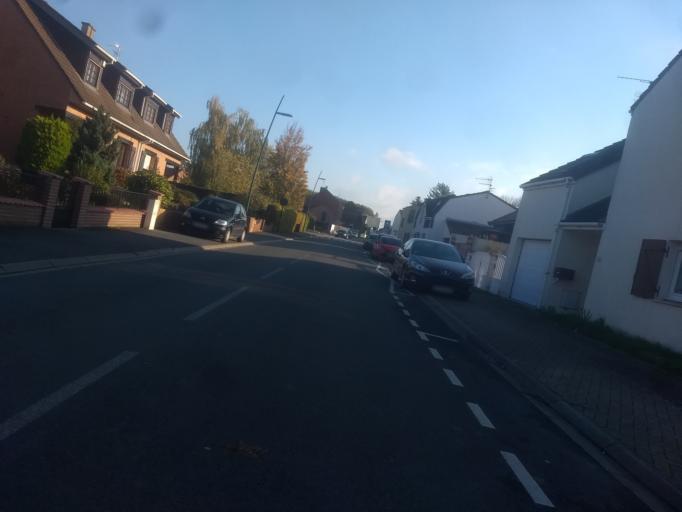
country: FR
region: Nord-Pas-de-Calais
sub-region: Departement du Pas-de-Calais
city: Tilloy-les-Mofflaines
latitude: 50.2768
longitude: 2.8135
